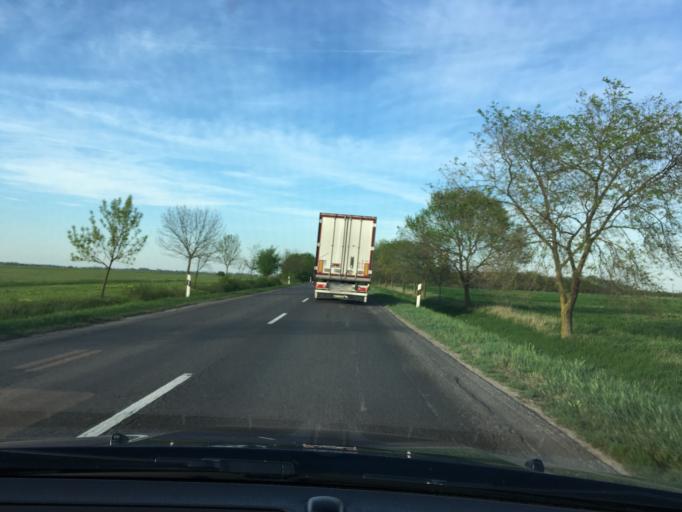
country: HU
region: Hajdu-Bihar
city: Berettyoujfalu
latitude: 47.1588
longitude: 21.5037
